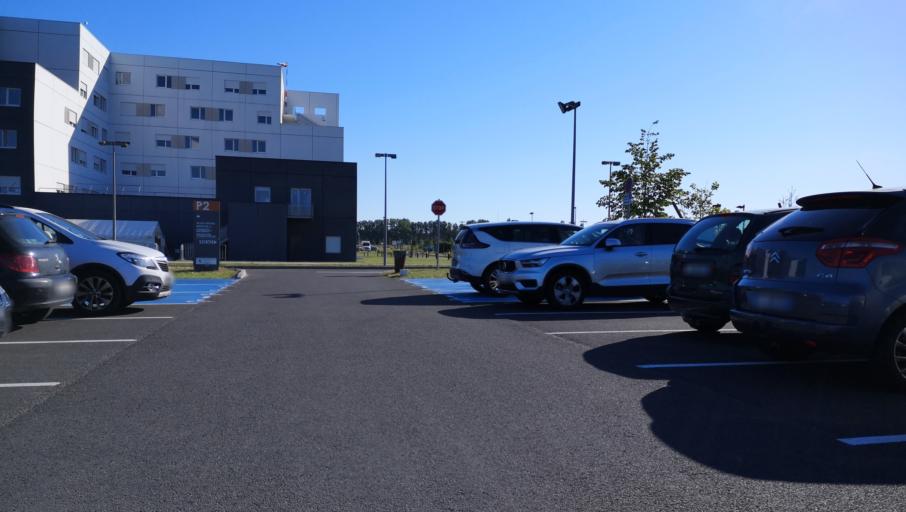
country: FR
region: Centre
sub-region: Departement du Loiret
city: Saran
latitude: 47.9387
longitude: 1.8784
